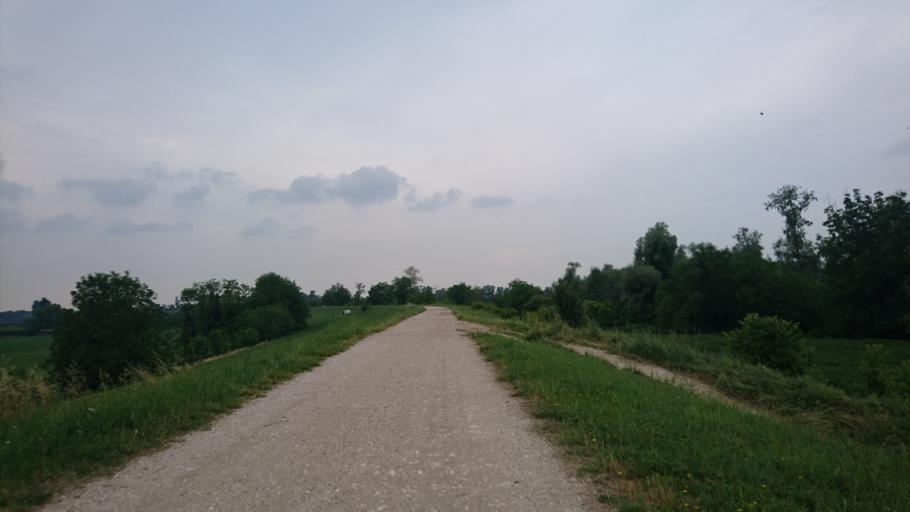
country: IT
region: Veneto
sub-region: Provincia di Padova
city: Masi
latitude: 45.1080
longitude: 11.5073
